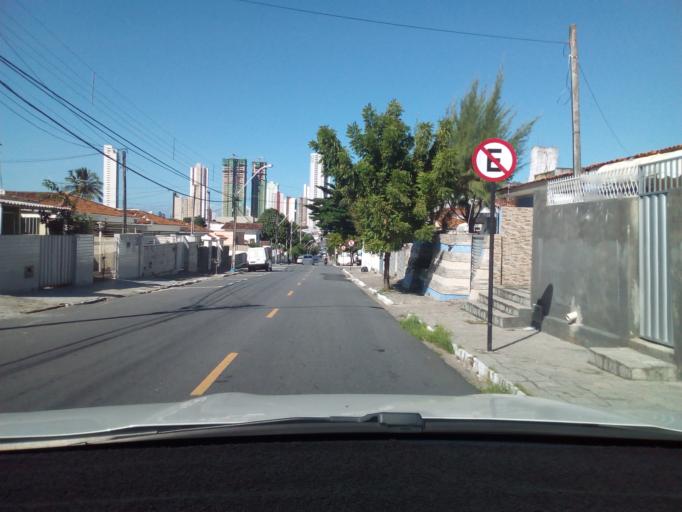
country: BR
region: Paraiba
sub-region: Joao Pessoa
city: Joao Pessoa
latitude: -7.1156
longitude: -34.8489
